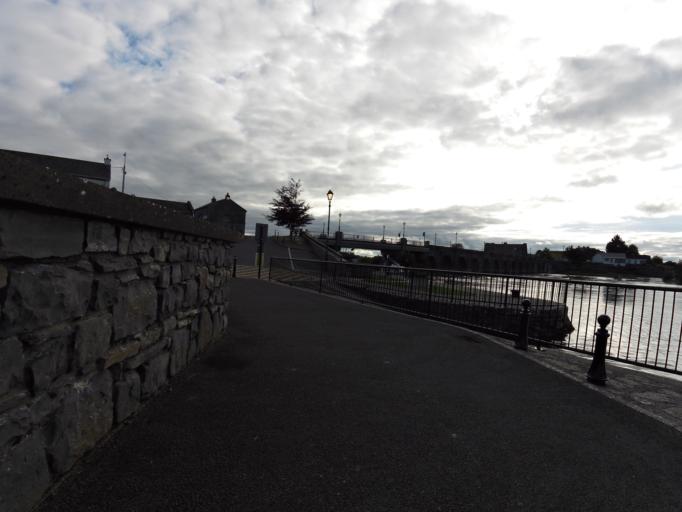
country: IE
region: Leinster
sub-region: Uibh Fhaili
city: Banagher
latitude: 53.2801
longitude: -8.0489
